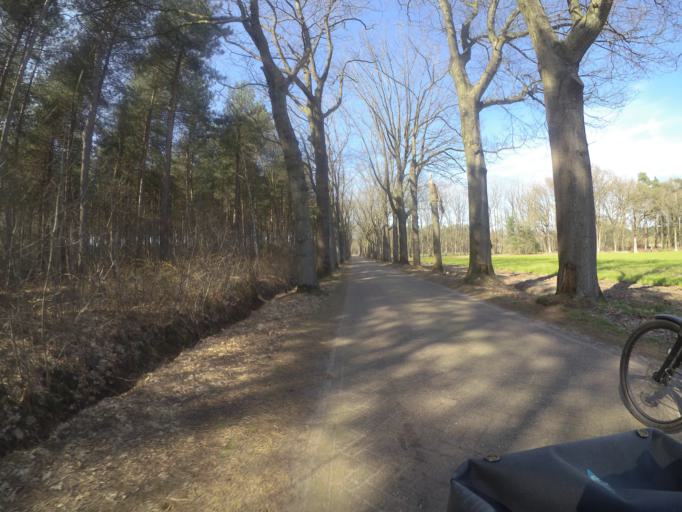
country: NL
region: North Brabant
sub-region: Gemeente Oirschot
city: Oostelbeers
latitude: 51.4804
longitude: 5.2577
